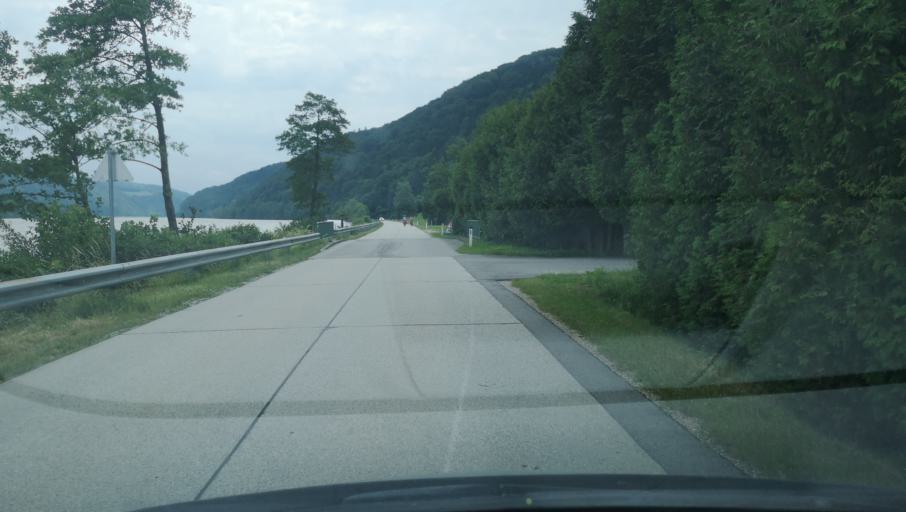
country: AT
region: Lower Austria
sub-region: Politischer Bezirk Melk
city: Nochling
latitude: 48.1915
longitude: 15.0133
